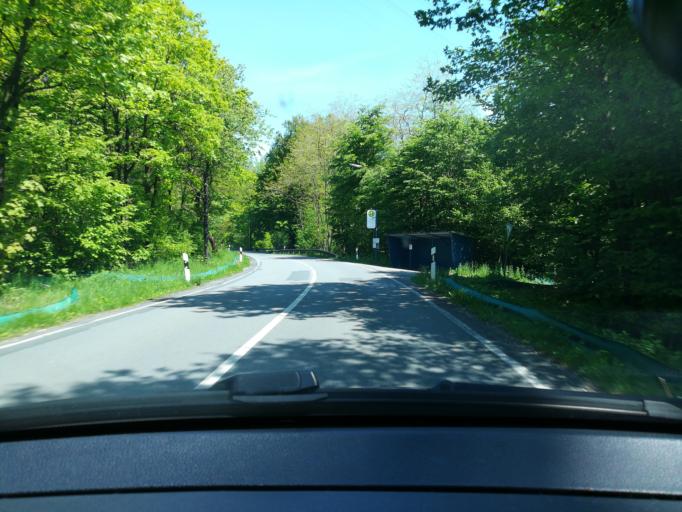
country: DE
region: North Rhine-Westphalia
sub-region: Regierungsbezirk Detmold
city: Oerlinghausen
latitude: 51.9706
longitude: 8.5994
